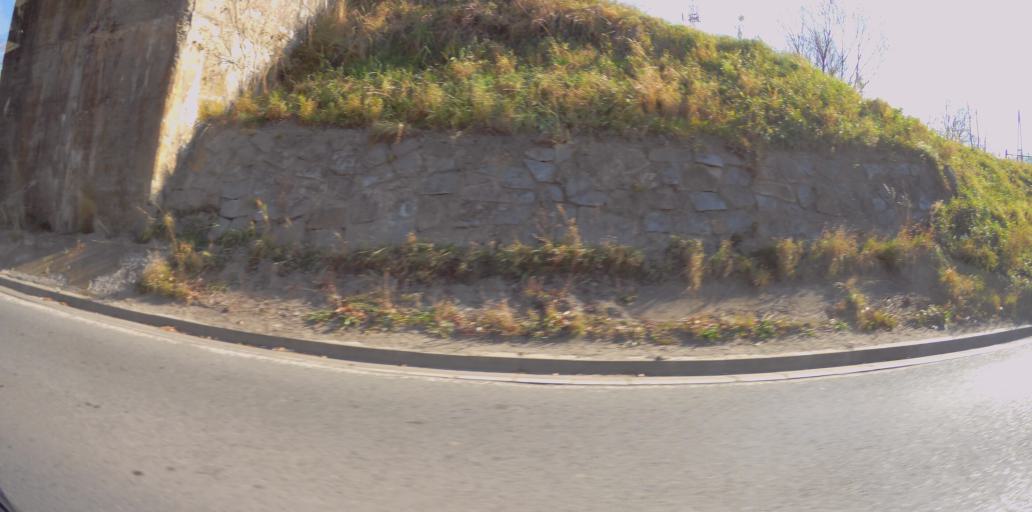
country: PL
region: Subcarpathian Voivodeship
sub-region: Powiat bieszczadzki
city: Ustrzyki Dolne
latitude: 49.4788
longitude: 22.6676
